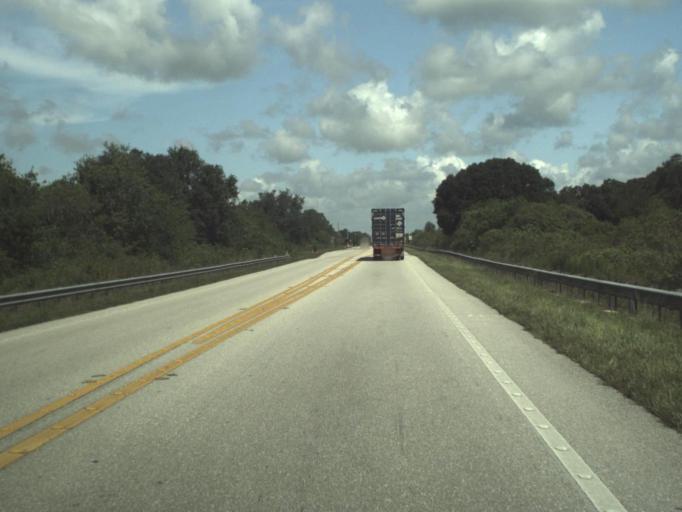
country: US
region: Florida
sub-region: Martin County
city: Indiantown
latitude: 27.0720
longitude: -80.5460
